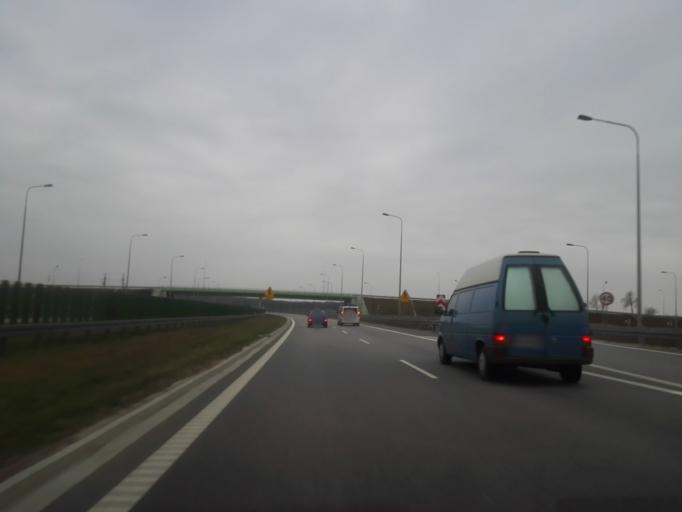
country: PL
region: Podlasie
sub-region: Powiat kolnenski
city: Stawiski
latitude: 53.3882
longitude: 22.1454
